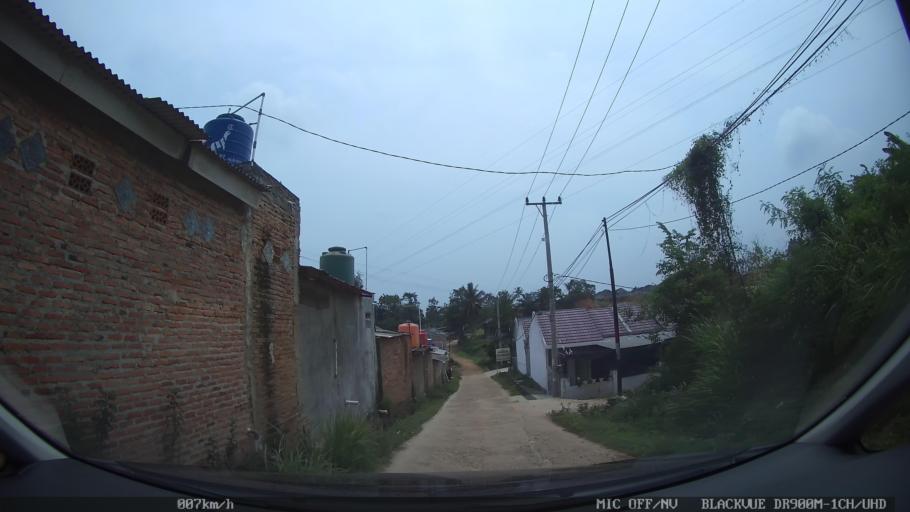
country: ID
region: Lampung
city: Kedaton
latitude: -5.4021
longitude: 105.3262
